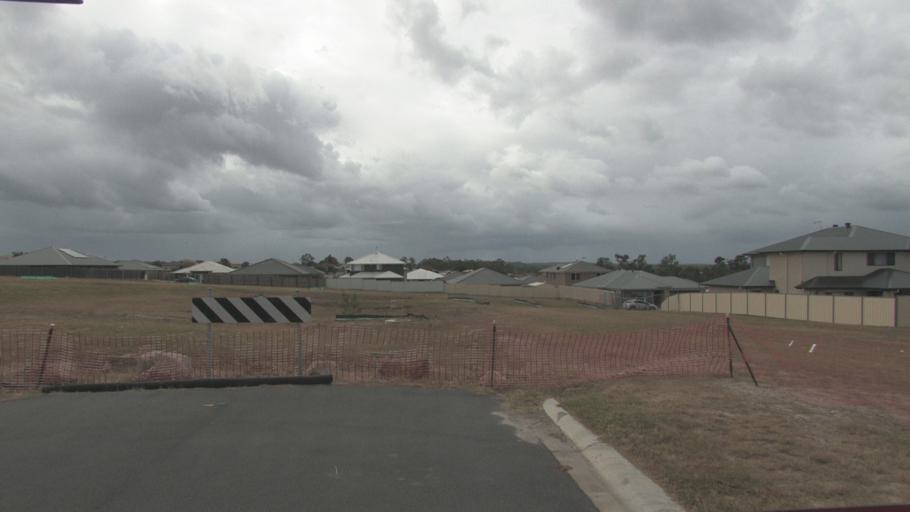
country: AU
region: Queensland
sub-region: Logan
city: Park Ridge South
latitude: -27.6867
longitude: 153.0471
